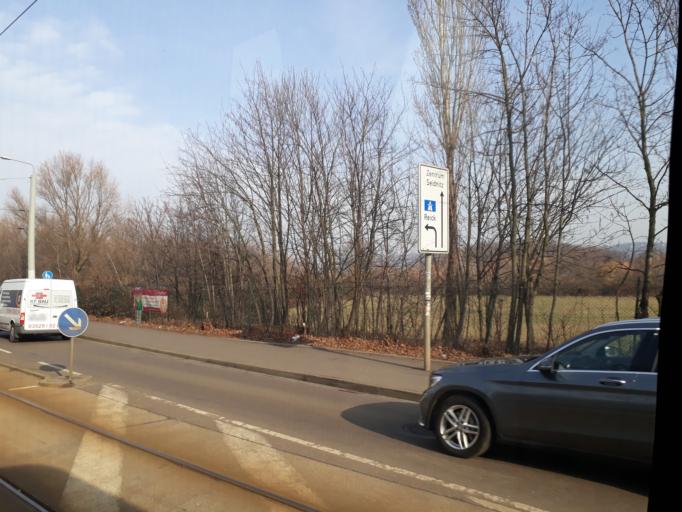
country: DE
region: Saxony
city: Heidenau
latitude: 51.0150
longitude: 13.8179
